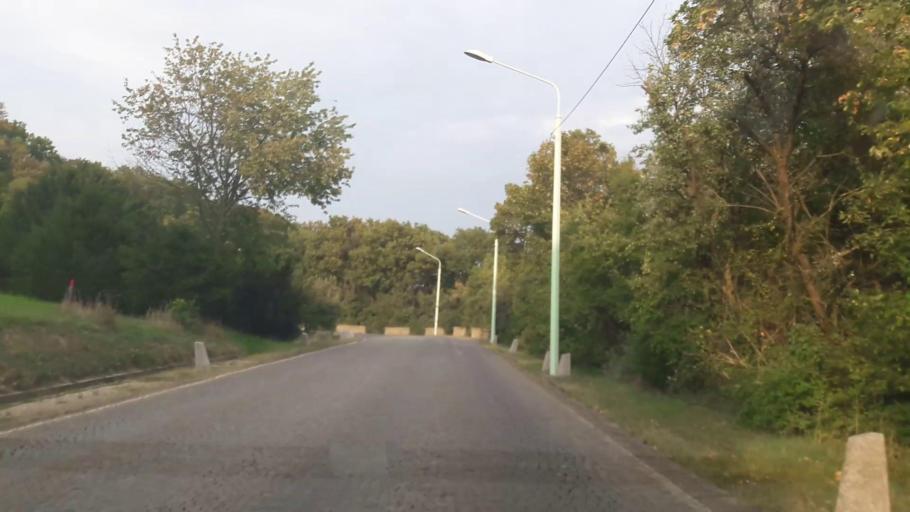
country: AT
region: Lower Austria
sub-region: Politischer Bezirk Wien-Umgebung
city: Klosterneuburg
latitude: 48.2688
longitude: 16.3261
